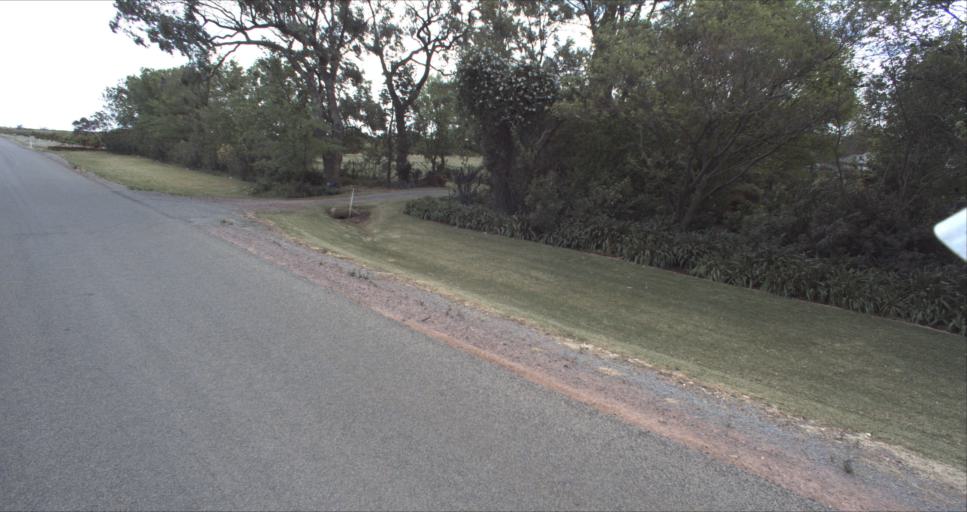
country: AU
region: New South Wales
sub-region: Leeton
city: Leeton
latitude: -34.5895
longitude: 146.3937
